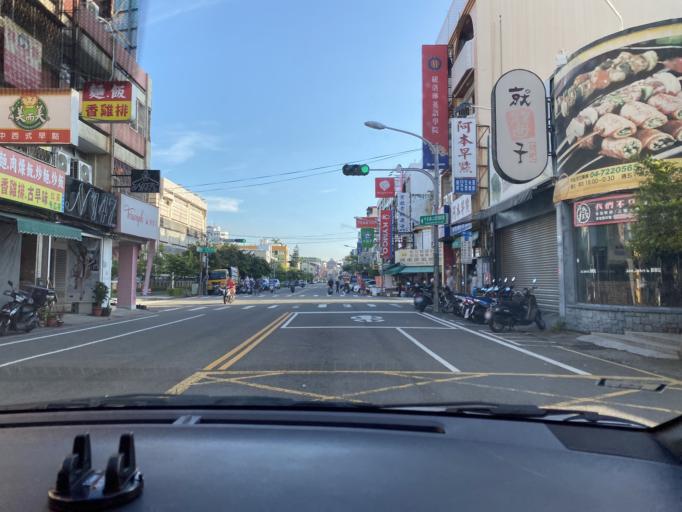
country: TW
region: Taiwan
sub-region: Changhua
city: Chang-hua
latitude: 24.0696
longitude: 120.5356
